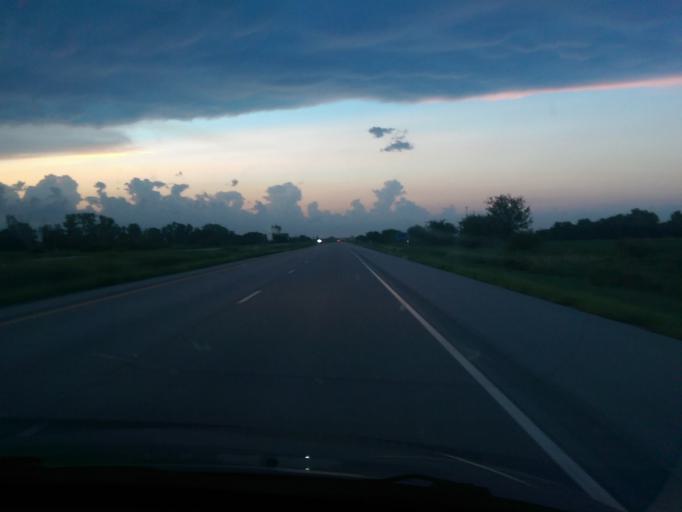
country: US
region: Nebraska
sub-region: Otoe County
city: Nebraska City
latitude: 40.7434
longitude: -95.8174
